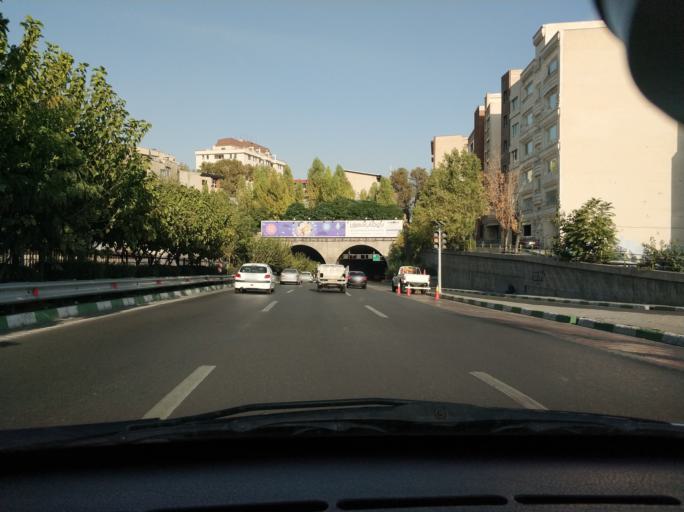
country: IR
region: Tehran
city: Tehran
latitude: 35.7437
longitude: 51.4030
